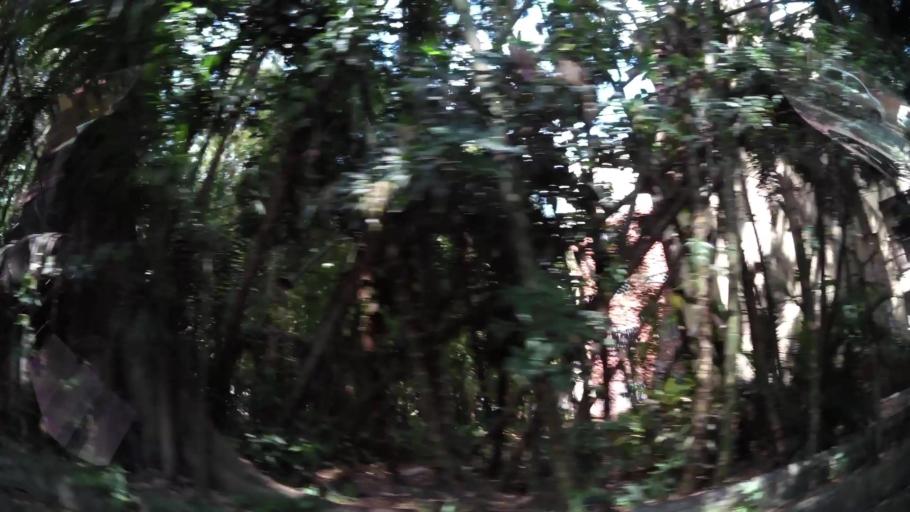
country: CO
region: Valle del Cauca
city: Cali
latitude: 3.4072
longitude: -76.5439
